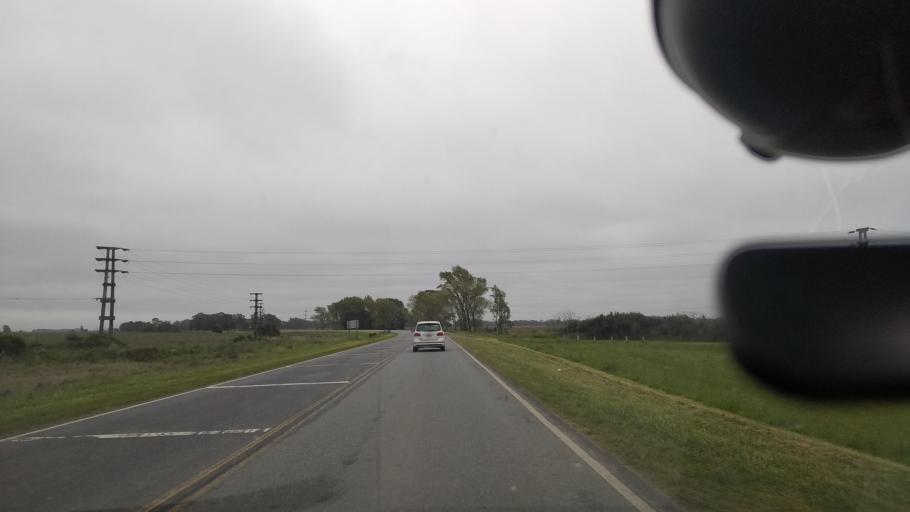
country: AR
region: Buenos Aires
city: Veronica
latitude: -35.3815
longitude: -57.3671
